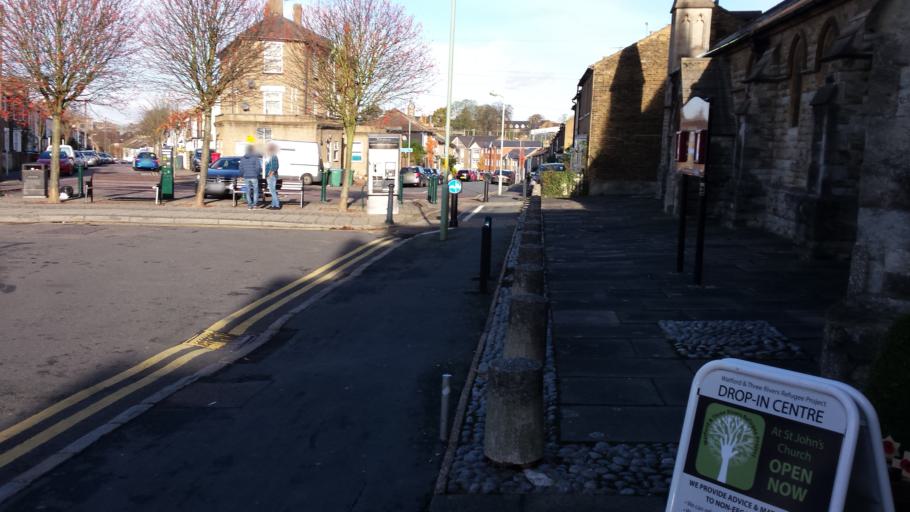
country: GB
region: England
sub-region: Hertfordshire
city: Watford
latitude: 51.6585
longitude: -0.3941
